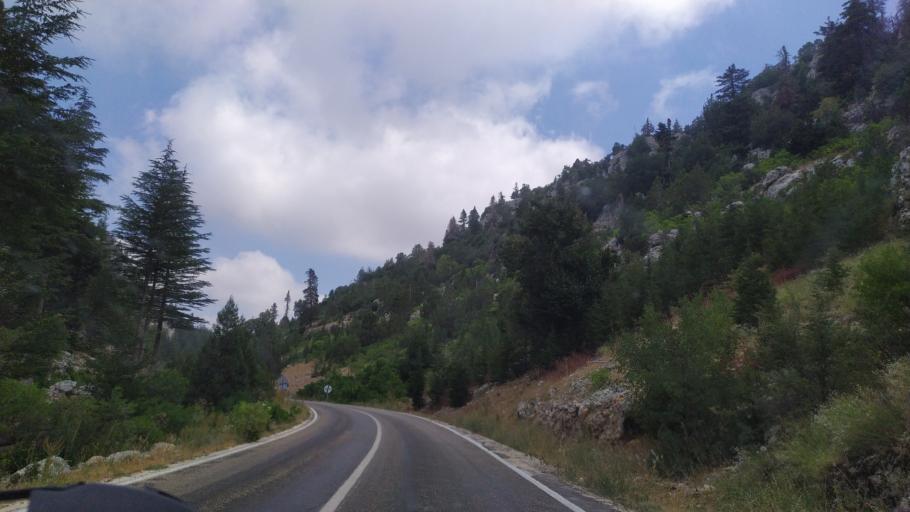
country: TR
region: Mersin
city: Kirobasi
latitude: 36.6077
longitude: 33.8836
